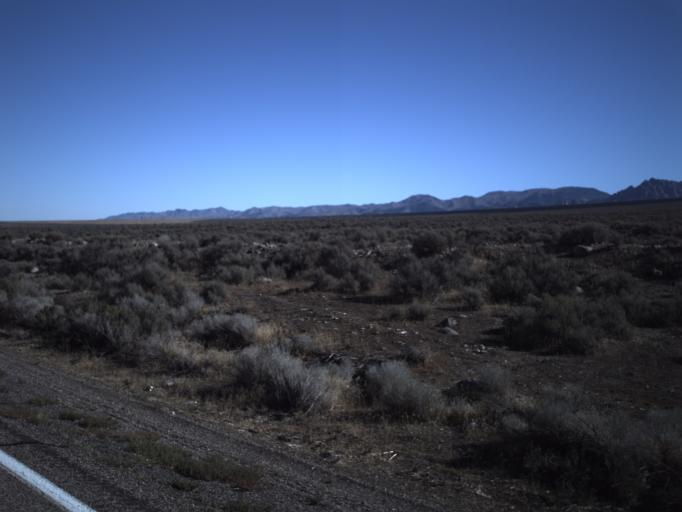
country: US
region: Utah
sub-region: Beaver County
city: Milford
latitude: 38.3074
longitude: -112.9695
